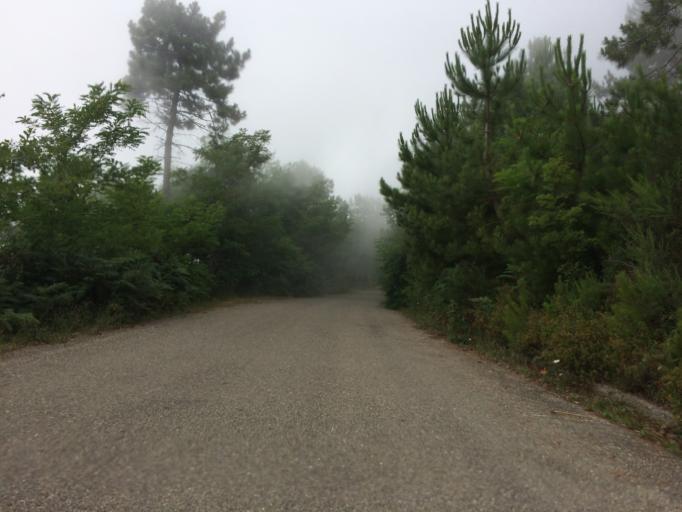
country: IT
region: Liguria
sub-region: Provincia di Imperia
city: Ceriana
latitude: 43.8565
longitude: 7.7430
